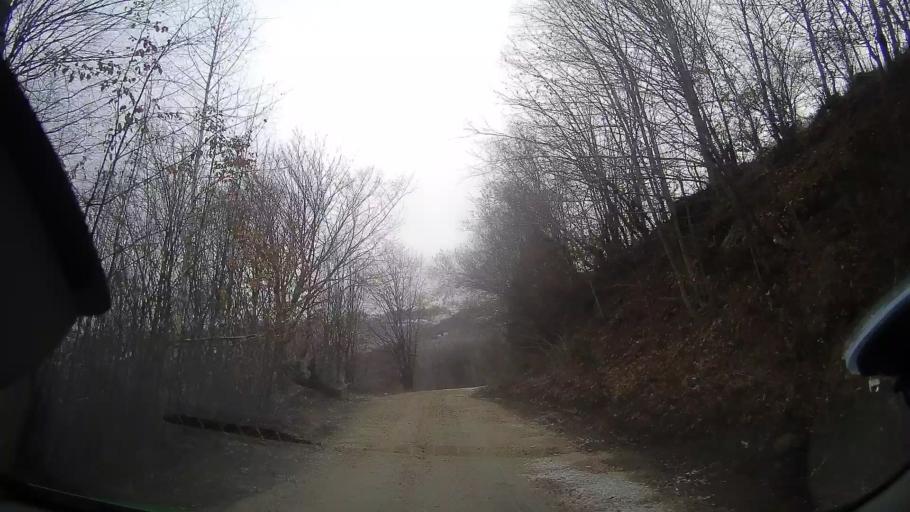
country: RO
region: Cluj
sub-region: Comuna Maguri-Racatau
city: Maguri-Racatau
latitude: 46.6549
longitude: 23.1881
